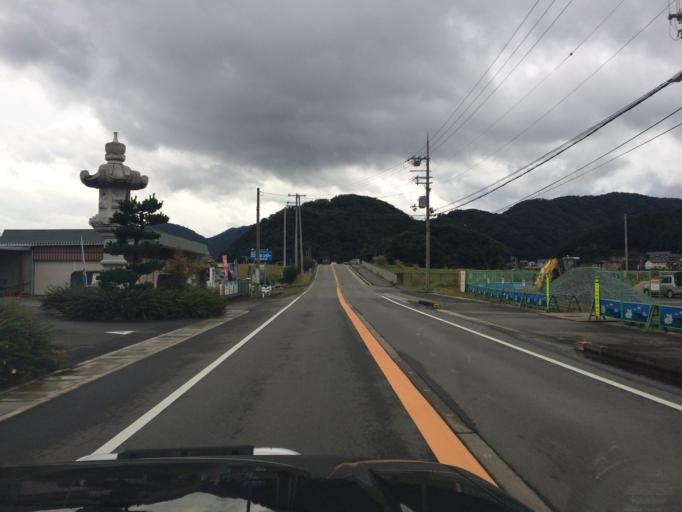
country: JP
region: Hyogo
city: Toyooka
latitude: 35.4590
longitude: 134.7728
